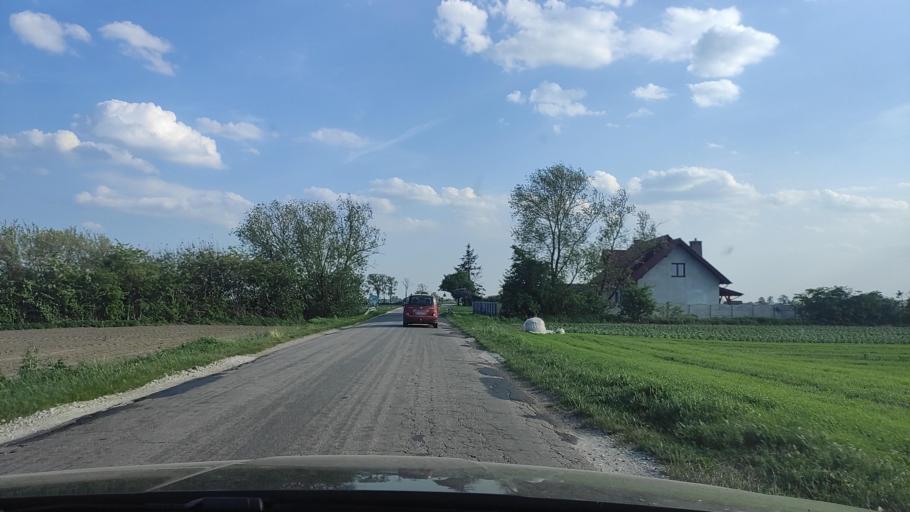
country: PL
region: Greater Poland Voivodeship
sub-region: Powiat poznanski
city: Kleszczewo
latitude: 52.3718
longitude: 17.1674
